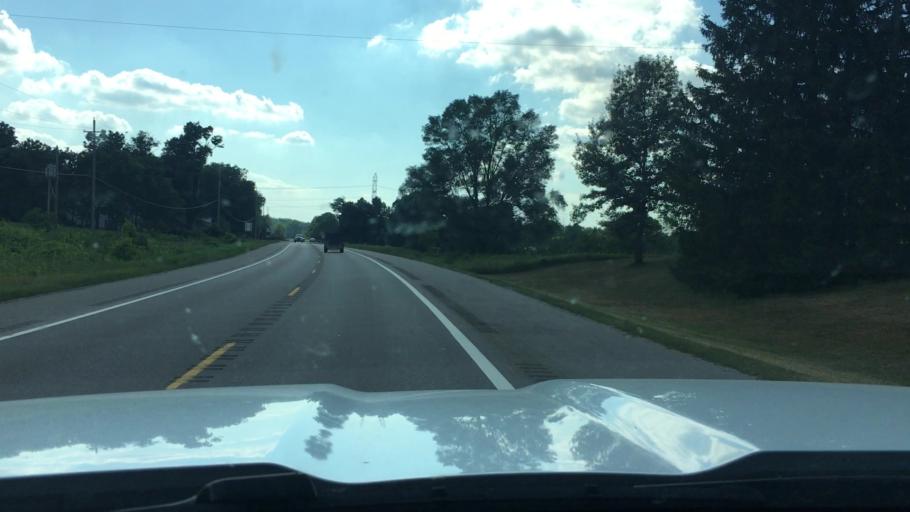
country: US
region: Michigan
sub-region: Kent County
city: Rockford
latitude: 43.0872
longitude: -85.4278
